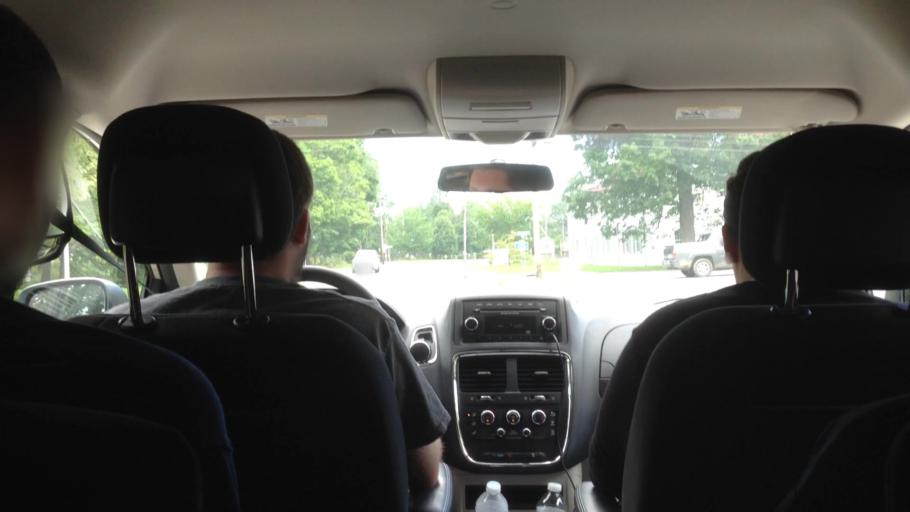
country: US
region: New York
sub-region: Dutchess County
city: Red Hook
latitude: 41.9967
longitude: -73.8745
